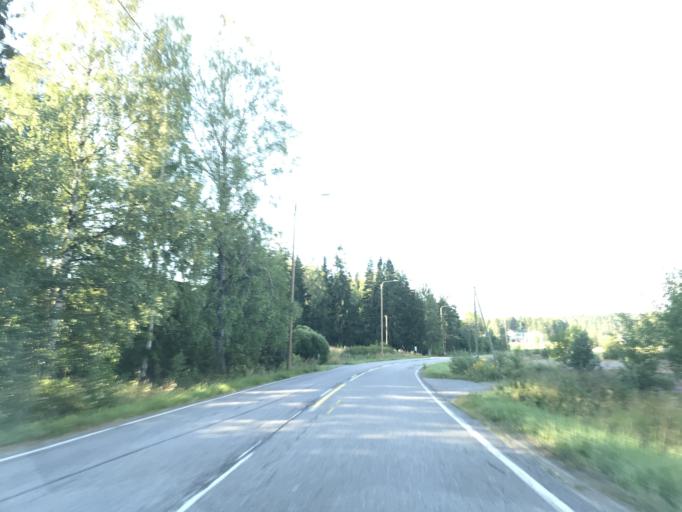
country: FI
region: Uusimaa
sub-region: Helsinki
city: Nurmijaervi
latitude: 60.3671
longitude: 24.6825
